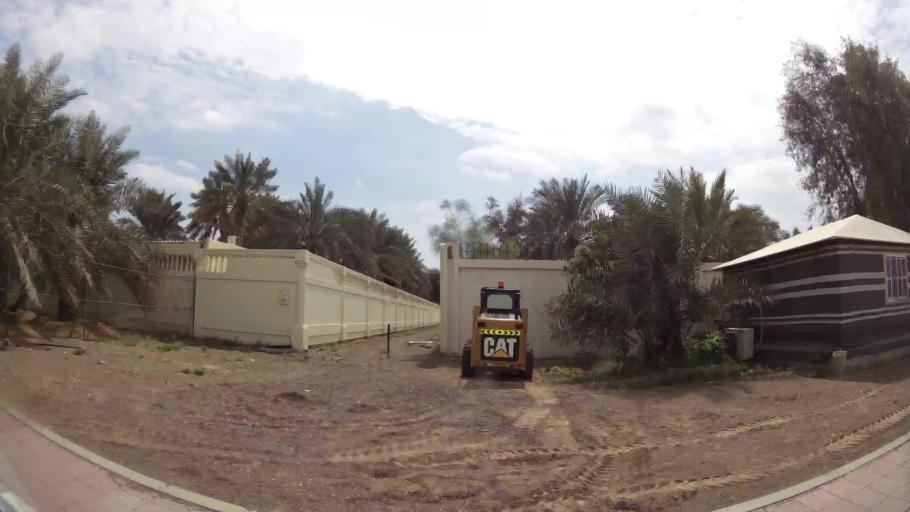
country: AE
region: Abu Dhabi
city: Al Ain
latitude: 24.2041
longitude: 55.7935
